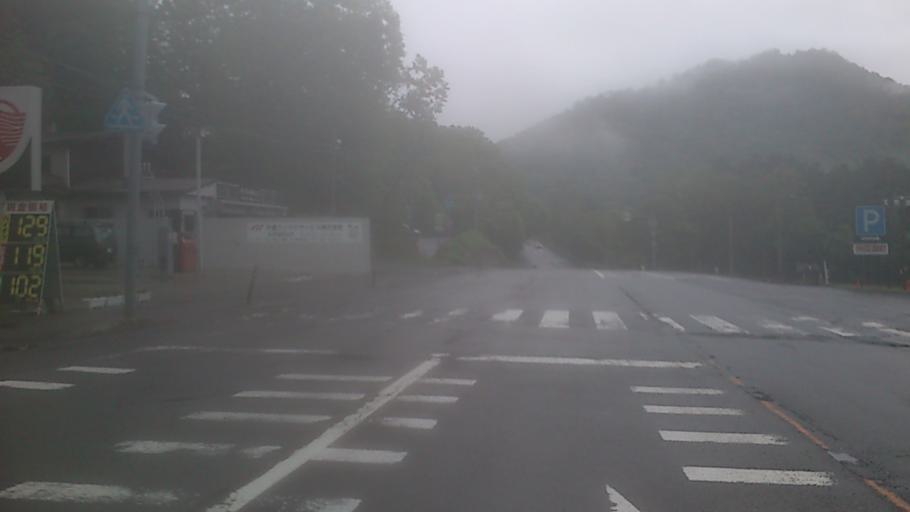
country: JP
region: Hokkaido
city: Shiraoi
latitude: 42.7748
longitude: 141.4049
